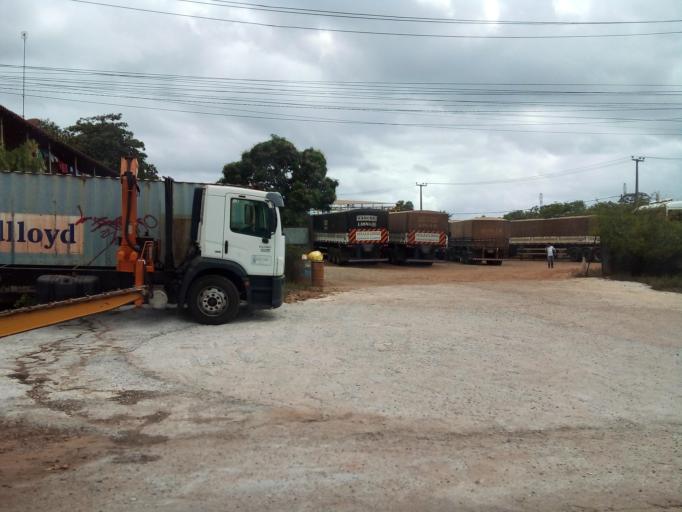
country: BR
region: Maranhao
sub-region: Sao Luis
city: Sao Luis
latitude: -2.6740
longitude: -44.2965
